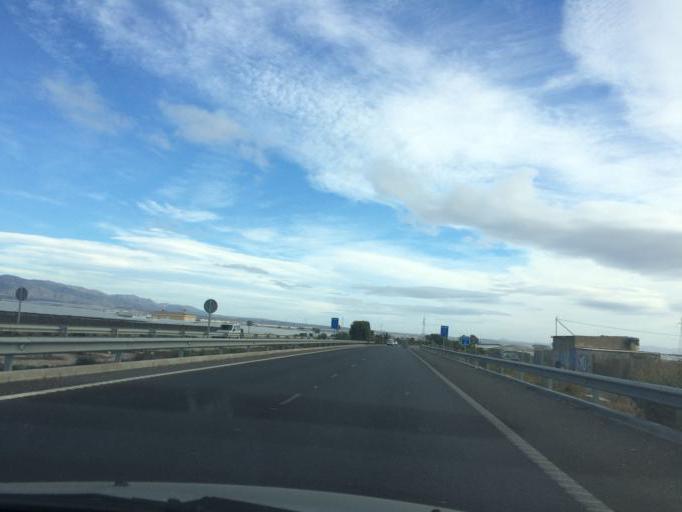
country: ES
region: Andalusia
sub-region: Provincia de Almeria
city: Almeria
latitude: 36.8446
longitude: -2.4184
